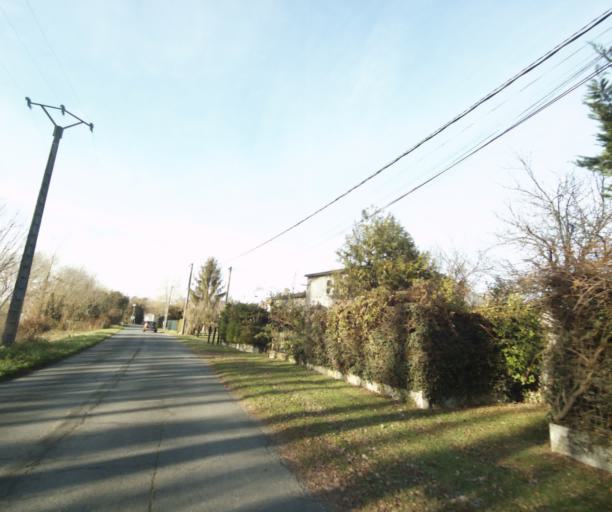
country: FR
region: Poitou-Charentes
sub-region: Departement de la Charente-Maritime
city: Chaniers
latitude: 45.7118
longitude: -0.5444
